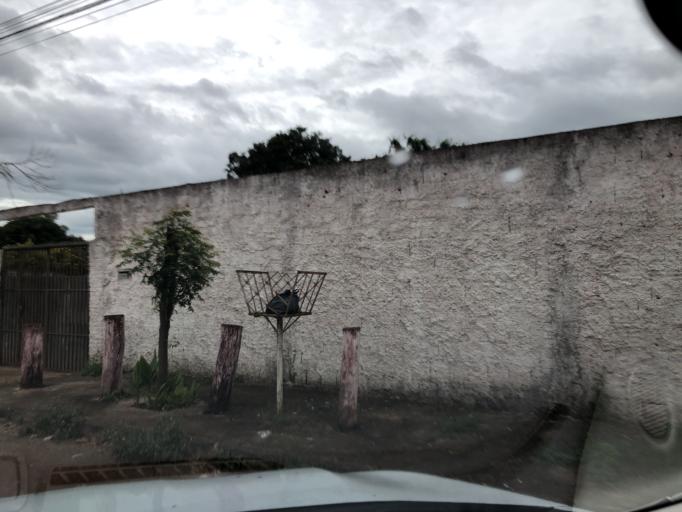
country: BR
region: Goias
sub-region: Luziania
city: Luziania
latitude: -16.1604
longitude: -47.9495
